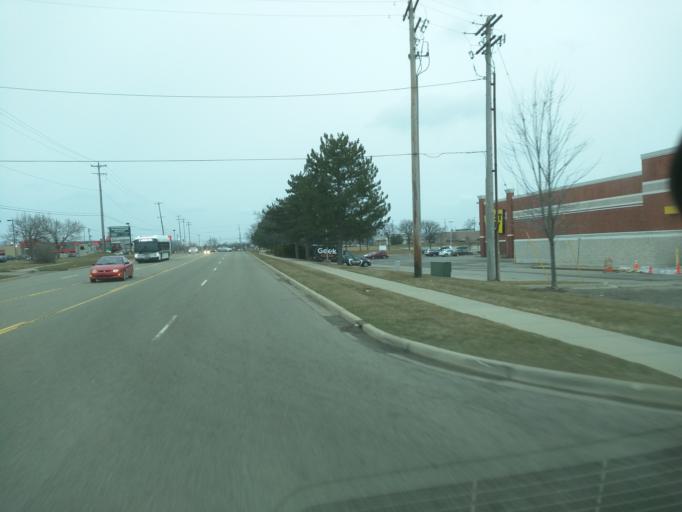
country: US
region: Michigan
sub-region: Eaton County
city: Waverly
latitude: 42.7442
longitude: -84.6226
